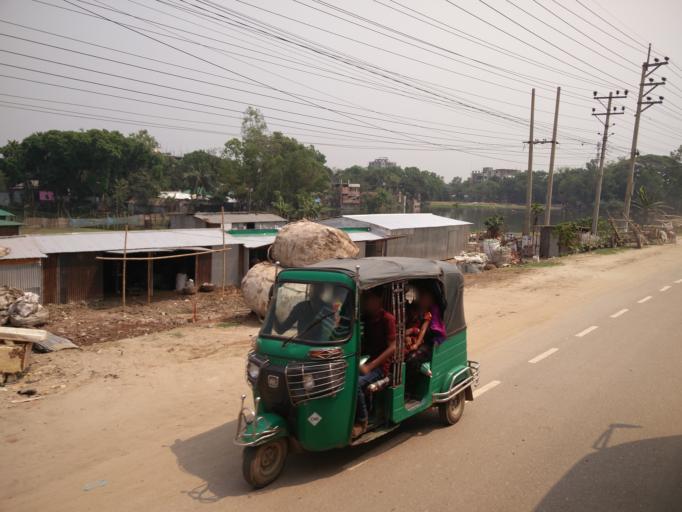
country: BD
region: Dhaka
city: Gafargaon
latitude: 24.4029
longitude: 90.3866
